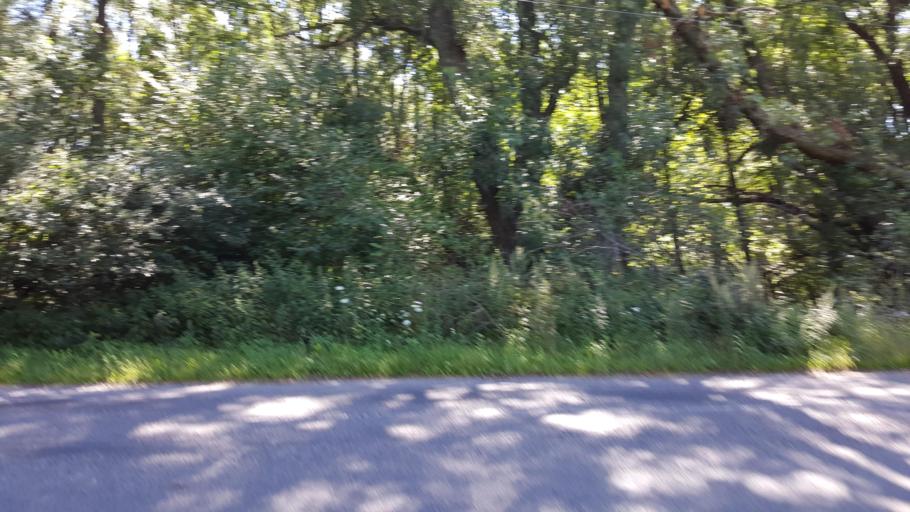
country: BY
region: Brest
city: Charnawchytsy
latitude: 52.3578
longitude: 23.6198
